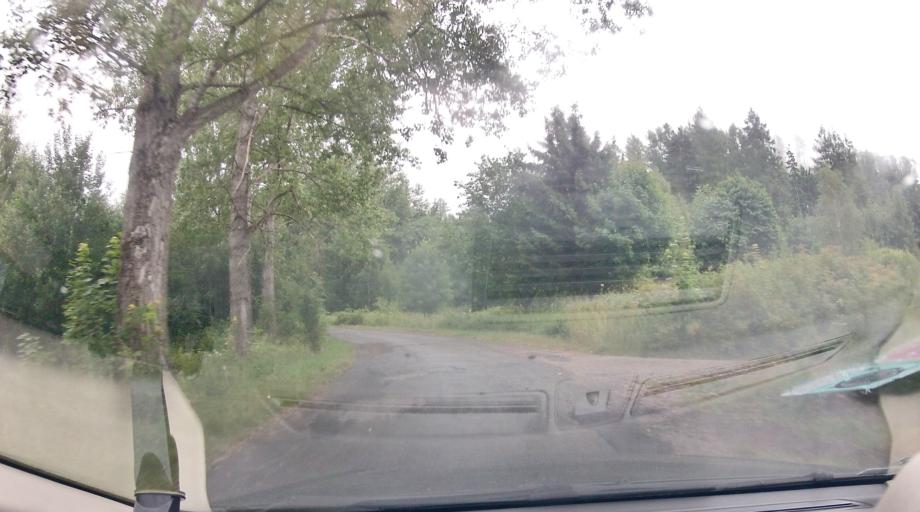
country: PL
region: Lower Silesian Voivodeship
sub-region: Powiat klodzki
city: Miedzylesie
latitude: 50.1920
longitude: 16.7405
